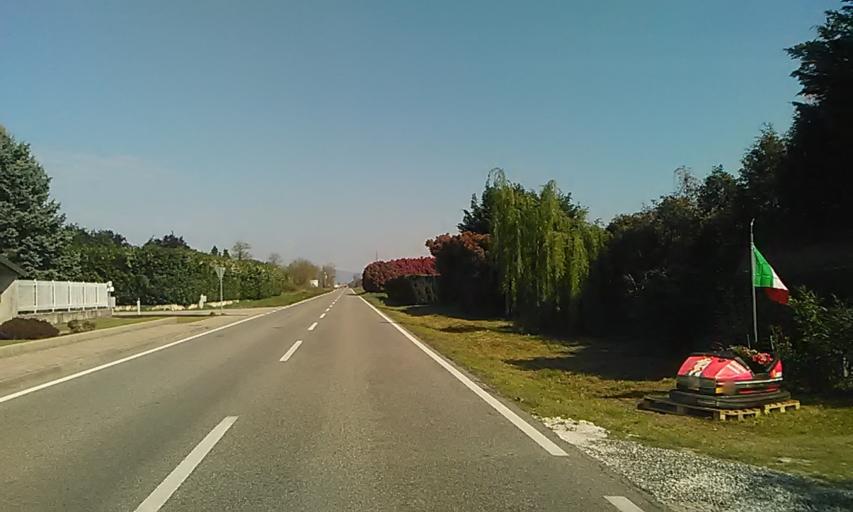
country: IT
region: Piedmont
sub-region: Provincia di Vercelli
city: Ghislarengo
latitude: 45.5373
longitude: 8.3855
